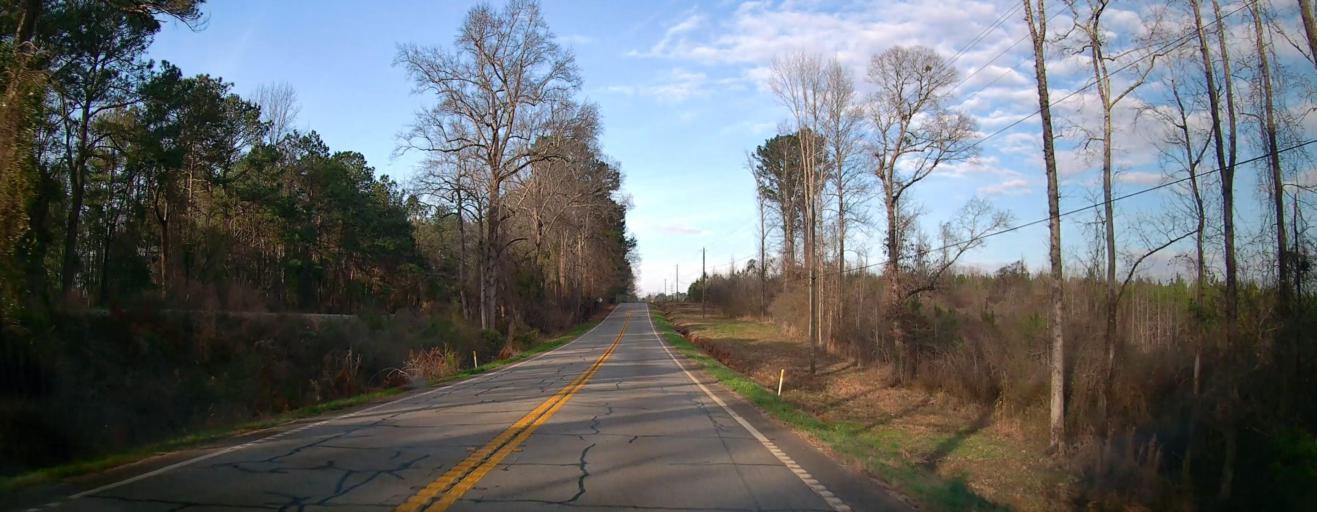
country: US
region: Georgia
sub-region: Harris County
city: Hamilton
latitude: 32.7328
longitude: -84.8736
